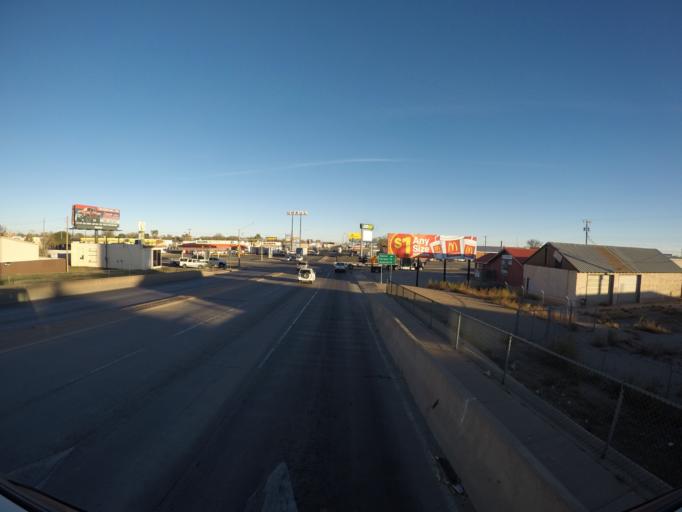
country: US
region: New Mexico
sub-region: Curry County
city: Clovis
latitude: 34.3979
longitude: -103.1964
